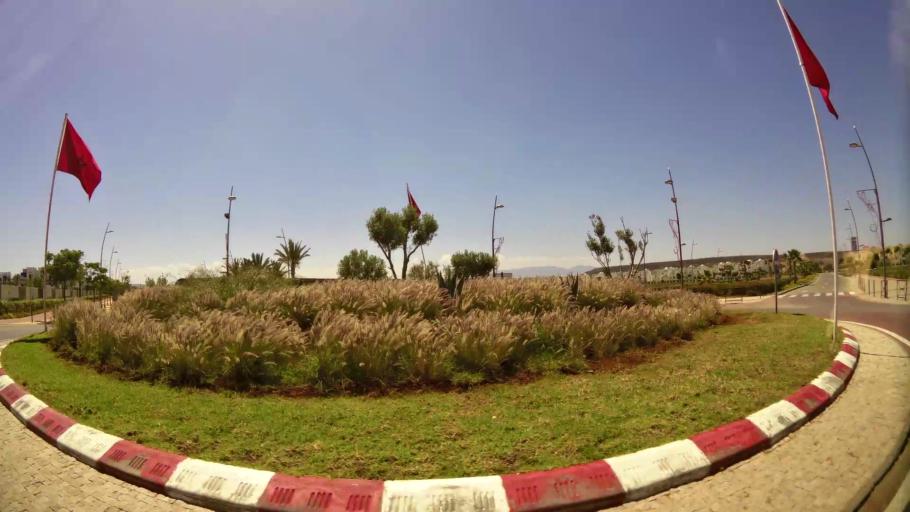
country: MA
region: Oriental
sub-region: Berkane-Taourirt
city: Madagh
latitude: 35.1019
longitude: -2.2989
